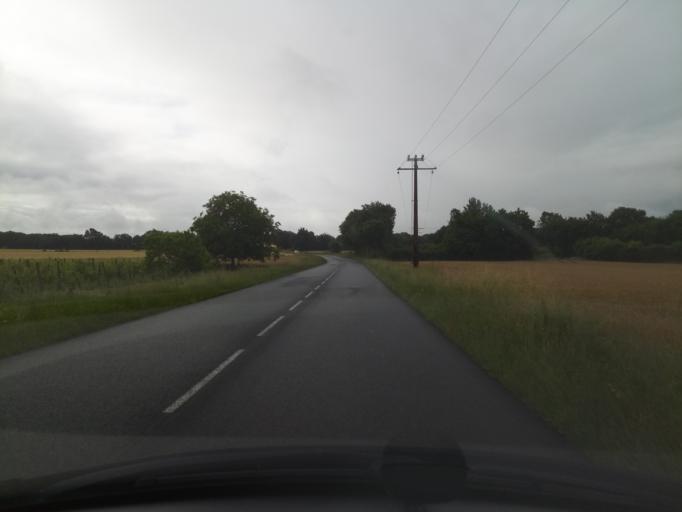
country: FR
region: Poitou-Charentes
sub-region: Departement de la Charente-Maritime
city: Saint-Germain-de-Marencennes
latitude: 46.1567
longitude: -0.8219
